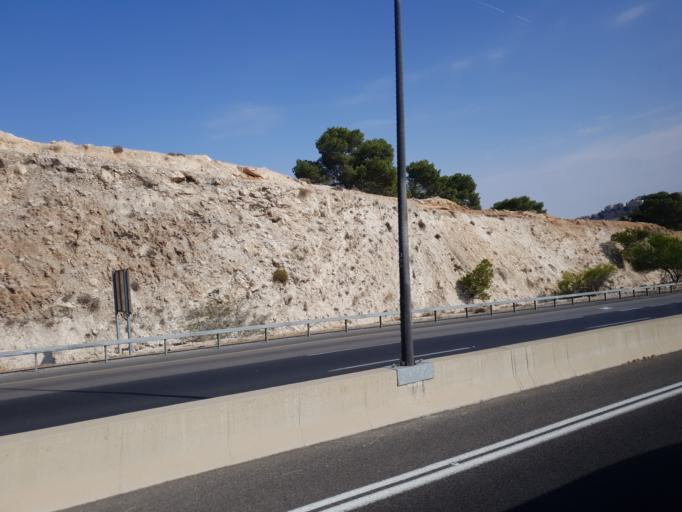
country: PS
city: Az Za`ayyim
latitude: 31.7839
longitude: 35.2856
